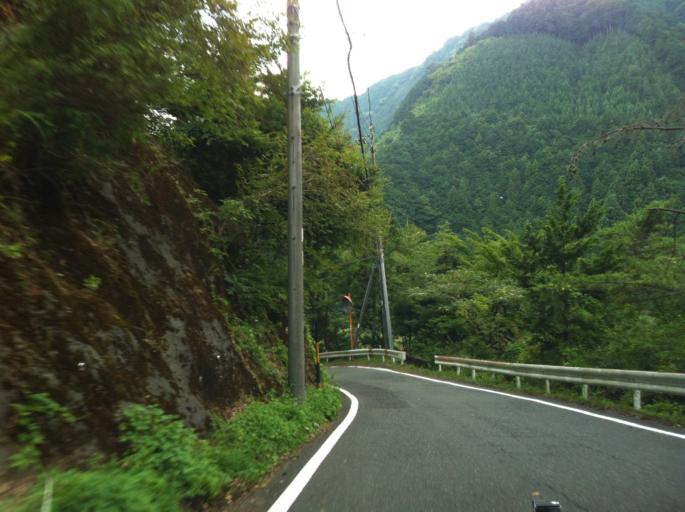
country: JP
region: Shizuoka
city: Shizuoka-shi
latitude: 35.2590
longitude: 138.3279
